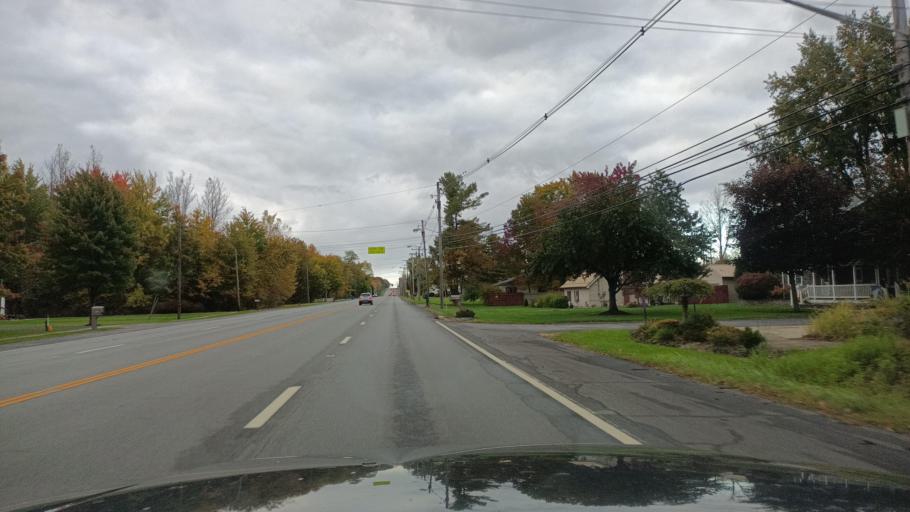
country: US
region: Ohio
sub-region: Trumbull County
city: Lordstown
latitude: 41.1711
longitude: -80.8574
